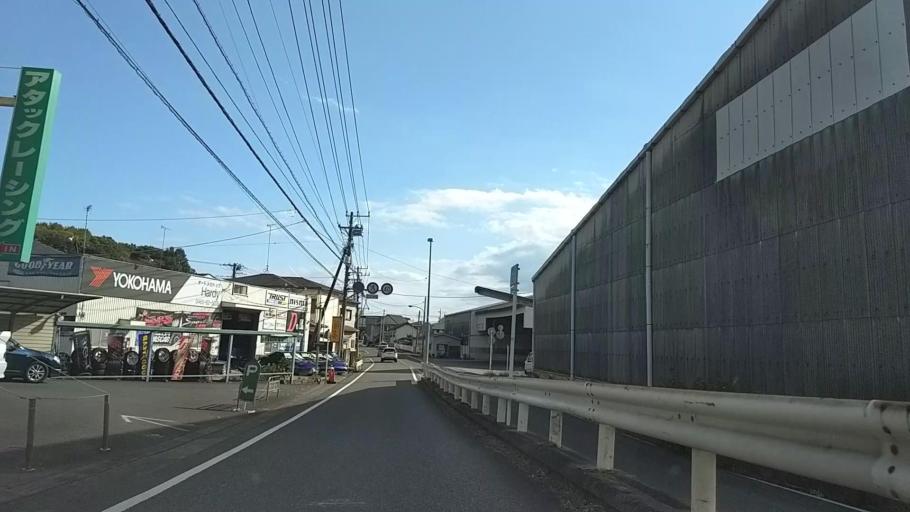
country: JP
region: Kanagawa
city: Odawara
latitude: 35.3273
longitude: 139.1587
